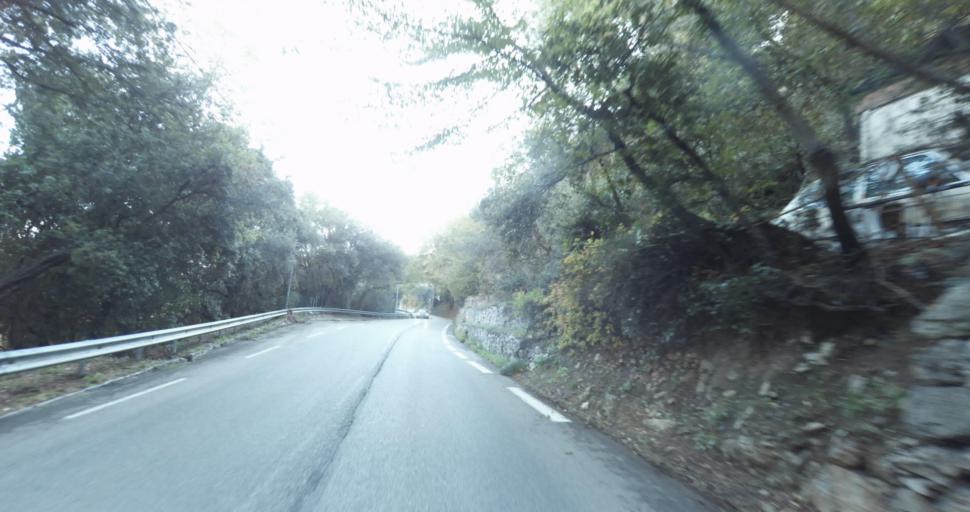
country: FR
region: Provence-Alpes-Cote d'Azur
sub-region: Departement des Alpes-Maritimes
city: Saint-Jeannet
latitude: 43.7454
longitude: 7.1307
